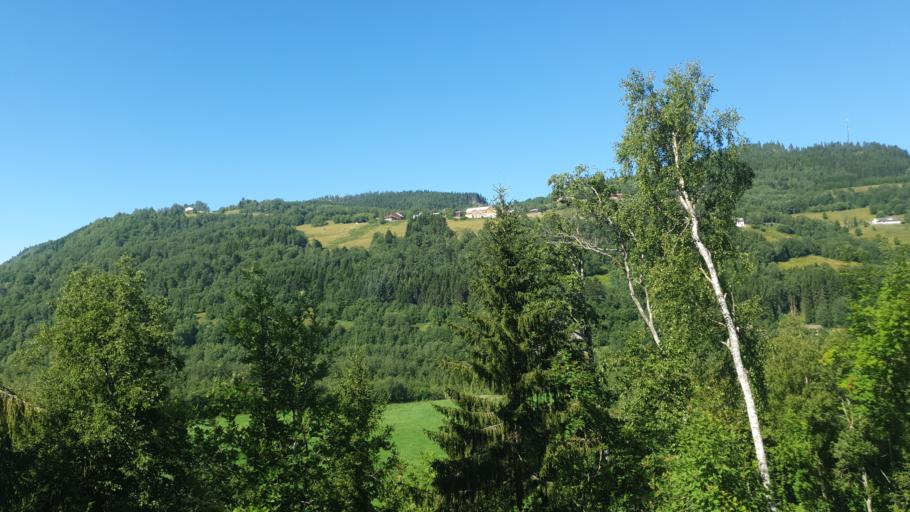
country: NO
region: Sor-Trondelag
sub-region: Meldal
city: Meldal
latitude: 63.1656
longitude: 9.7351
